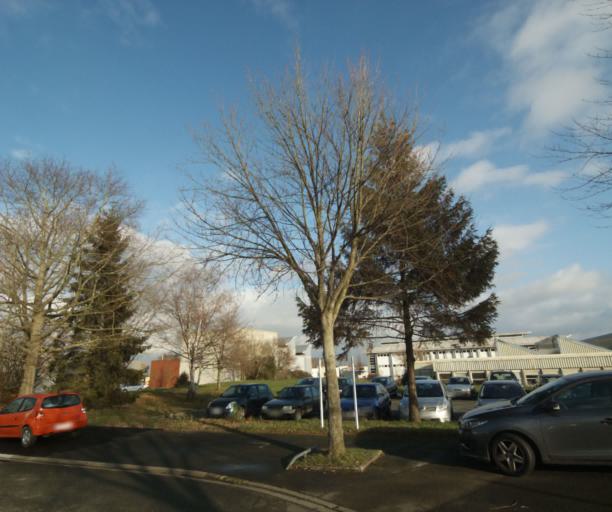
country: FR
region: Pays de la Loire
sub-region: Departement de la Sarthe
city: La Chapelle-Saint-Aubin
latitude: 48.0183
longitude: 0.1580
